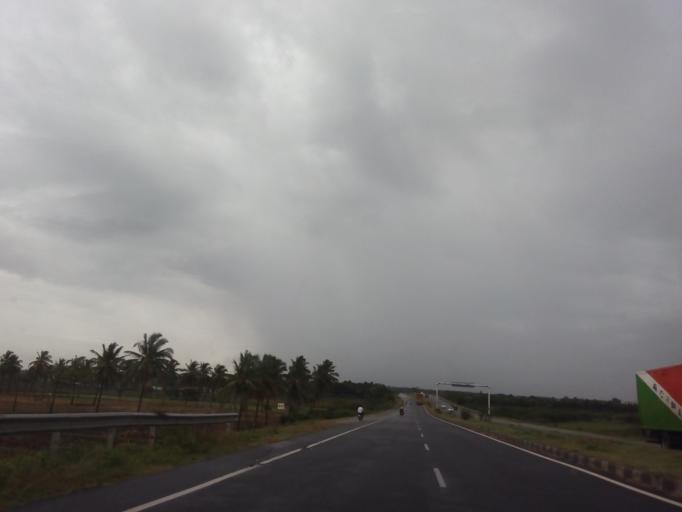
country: IN
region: Karnataka
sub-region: Davanagere
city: Harihar
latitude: 14.4338
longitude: 75.9412
